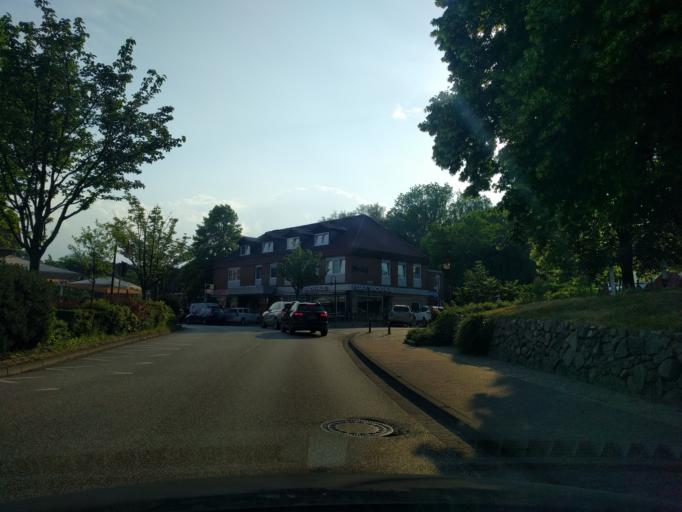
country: DE
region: Lower Saxony
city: Seevetal
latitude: 53.3864
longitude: 9.9827
